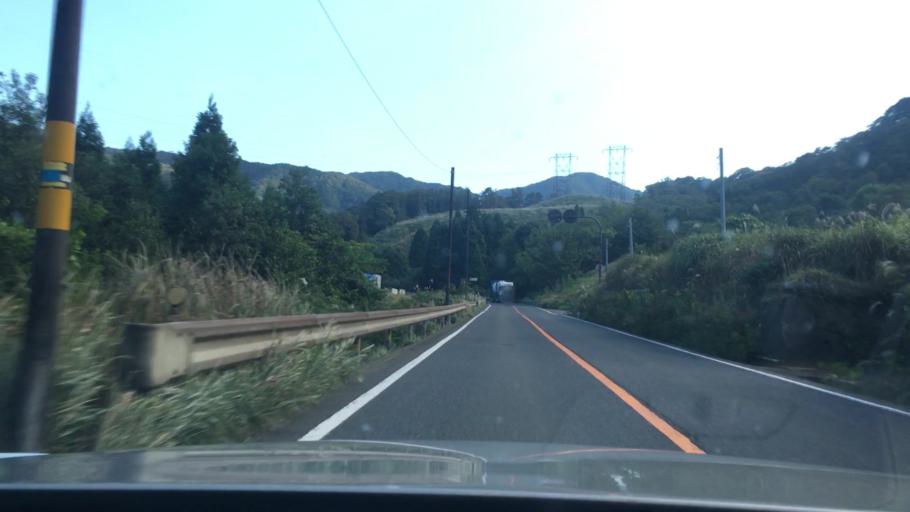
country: JP
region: Fukui
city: Tsuruga
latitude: 35.5882
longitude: 136.1006
